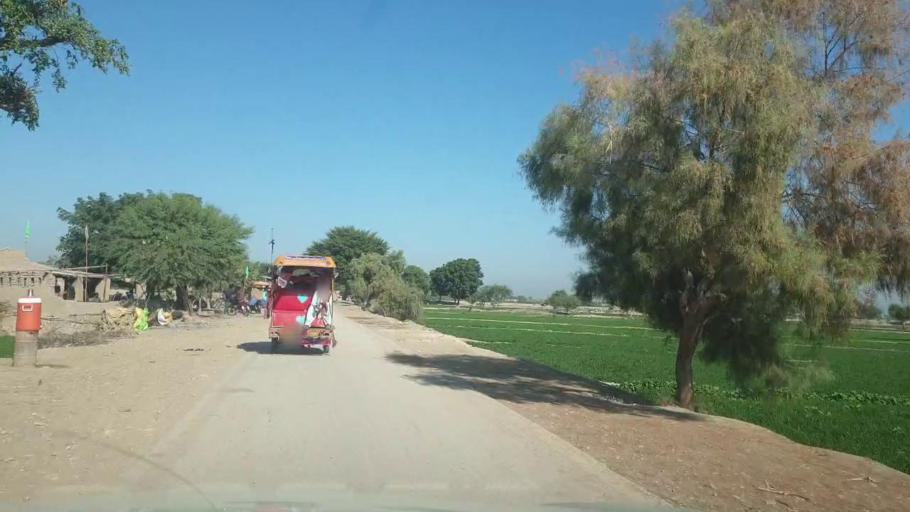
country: PK
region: Sindh
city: Bhan
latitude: 26.5535
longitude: 67.6334
